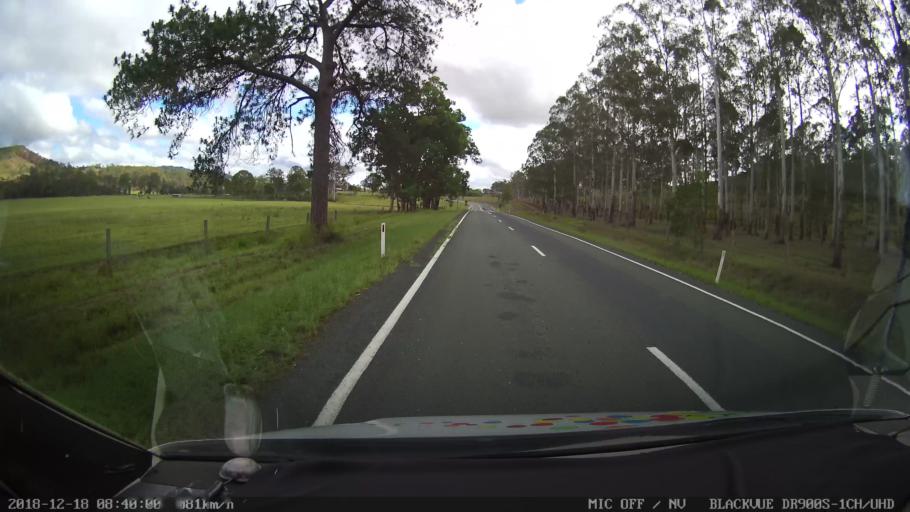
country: AU
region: Queensland
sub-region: Logan
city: Cedar Vale
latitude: -28.2469
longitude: 152.8441
